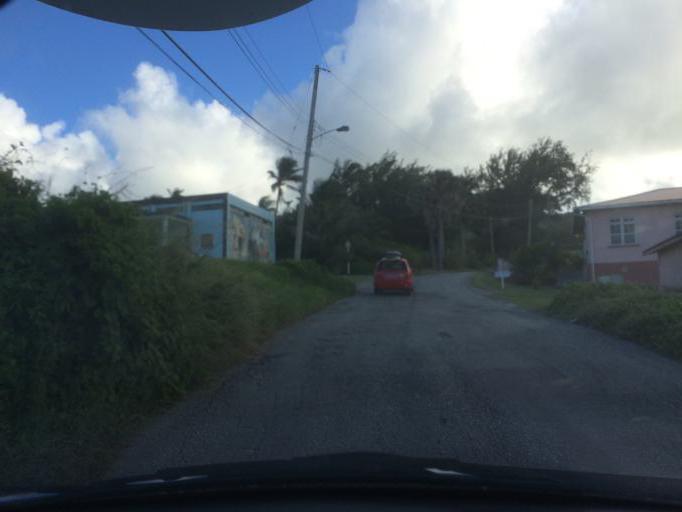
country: BB
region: Saint Joseph
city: Bathsheba
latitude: 13.2121
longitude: -59.5168
